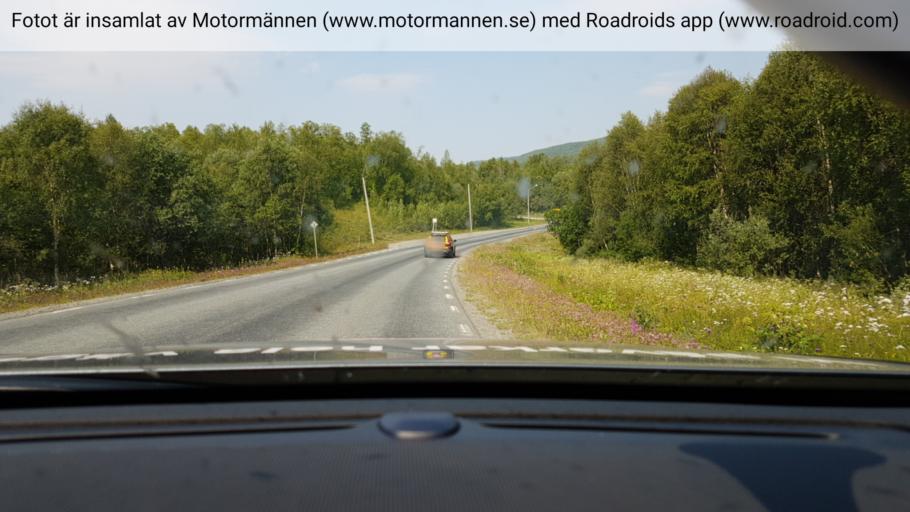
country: NO
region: Nordland
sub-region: Rana
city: Mo i Rana
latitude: 65.7378
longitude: 15.0929
